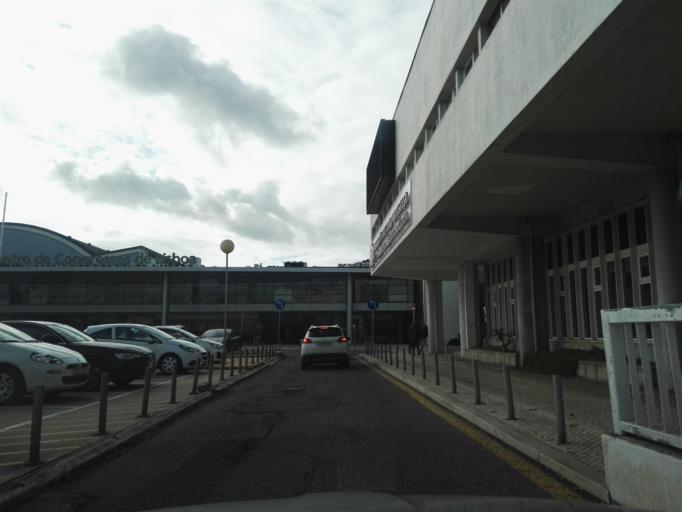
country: PT
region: Setubal
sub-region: Almada
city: Pragal
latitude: 38.6994
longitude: -9.1829
